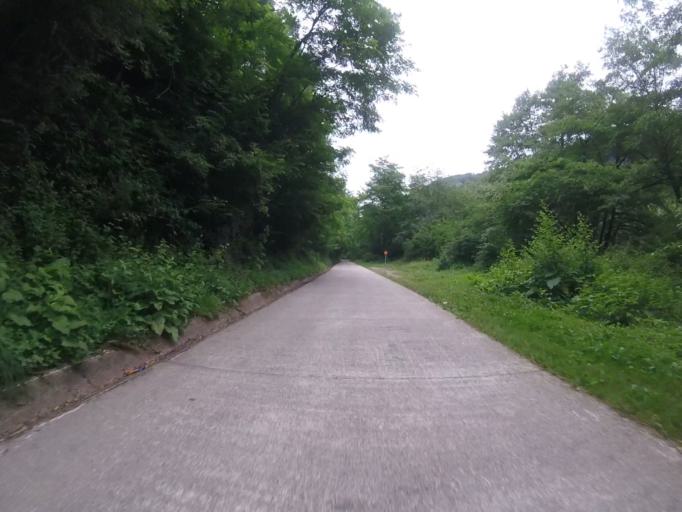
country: ES
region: Navarre
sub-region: Provincia de Navarra
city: Doneztebe
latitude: 43.1363
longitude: -1.6656
